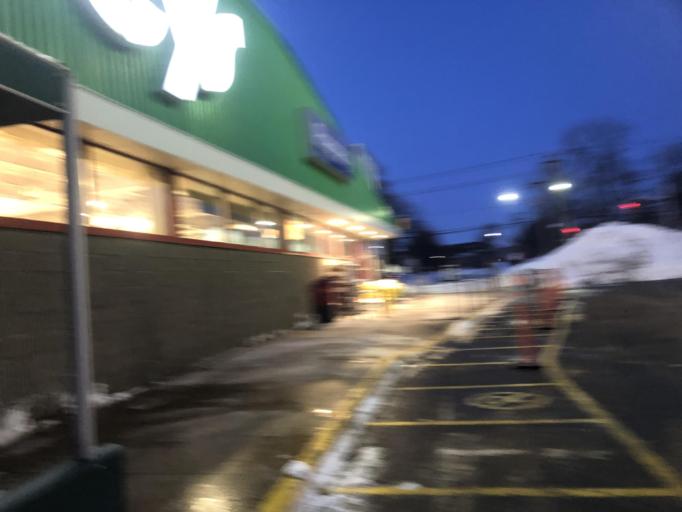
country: CA
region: New Brunswick
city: Saint John
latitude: 45.2795
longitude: -66.0782
